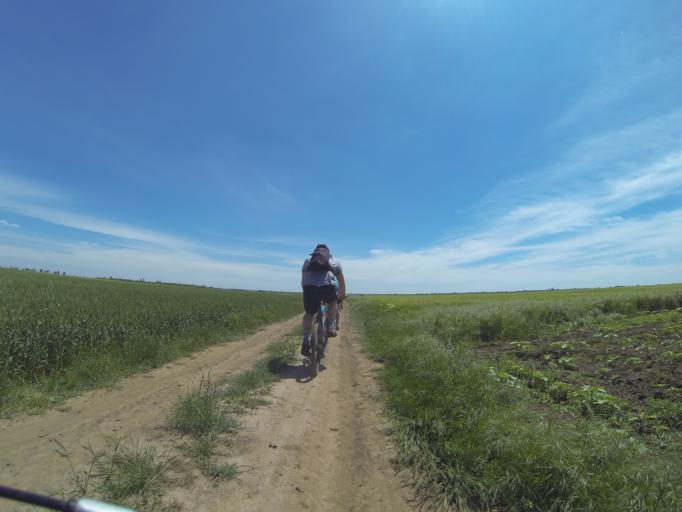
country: RO
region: Dolj
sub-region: Comuna Leu
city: Zanoaga
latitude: 44.1796
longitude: 24.0801
